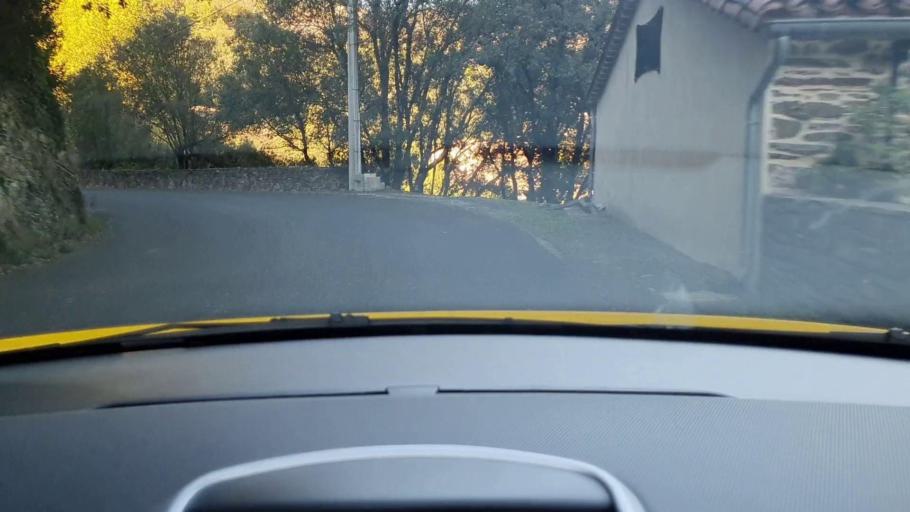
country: FR
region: Languedoc-Roussillon
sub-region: Departement du Gard
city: Sumene
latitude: 44.0043
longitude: 3.7109
